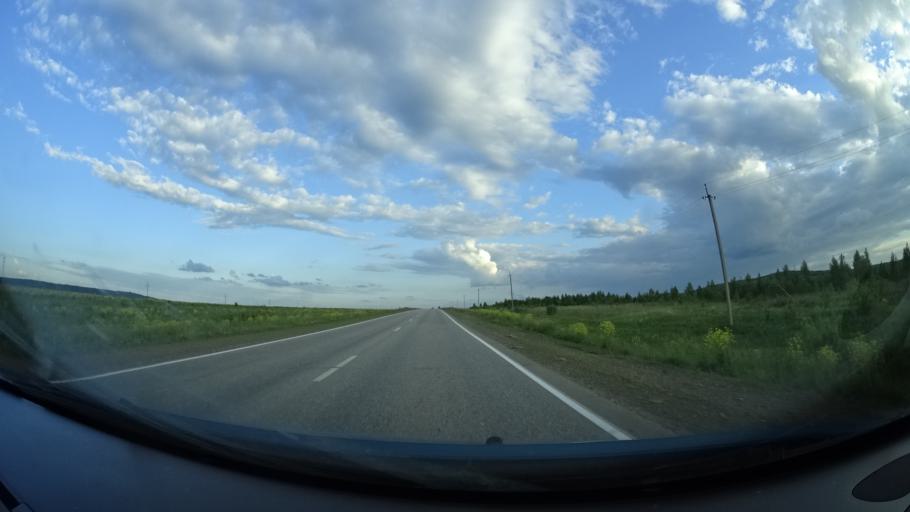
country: RU
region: Perm
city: Barda
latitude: 57.0535
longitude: 55.5438
